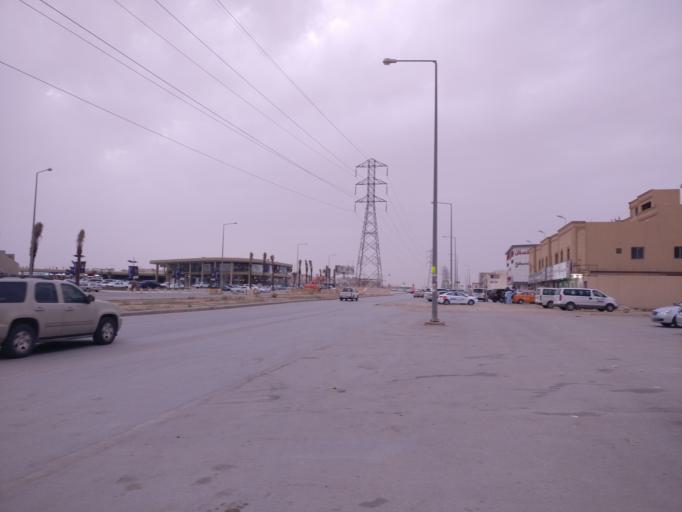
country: SA
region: Ar Riyad
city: Riyadh
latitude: 24.6859
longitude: 46.5842
